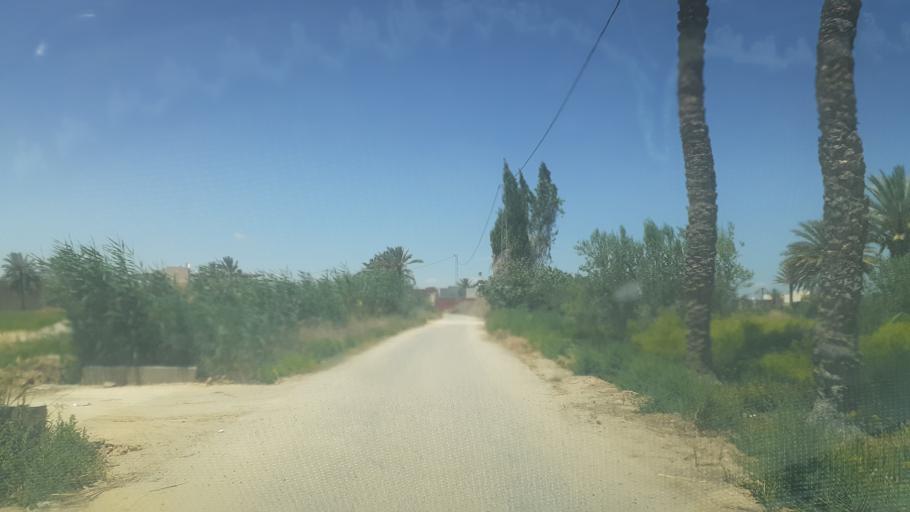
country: TN
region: Qabis
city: Gabes
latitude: 33.9288
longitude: 10.0602
